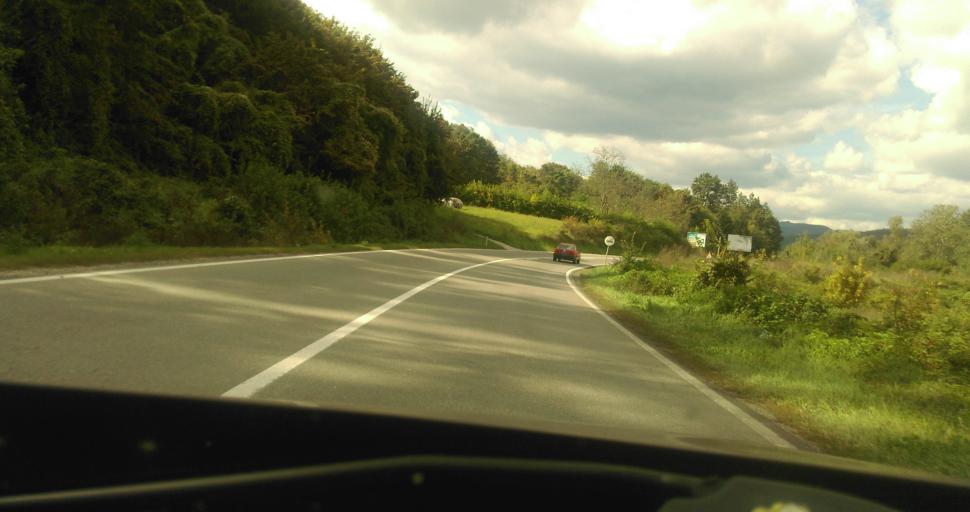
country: RS
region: Central Serbia
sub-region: Moravicki Okrug
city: Cacak
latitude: 43.8966
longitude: 20.2836
